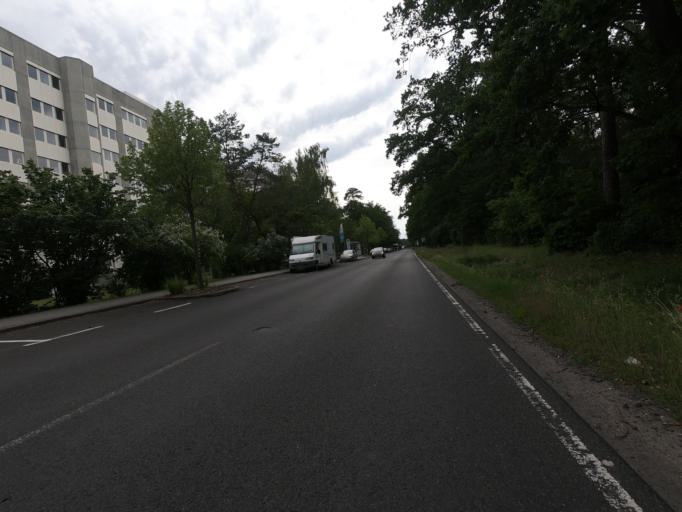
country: DE
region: Hesse
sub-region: Regierungsbezirk Darmstadt
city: Neu Isenburg
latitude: 50.0533
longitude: 8.6566
